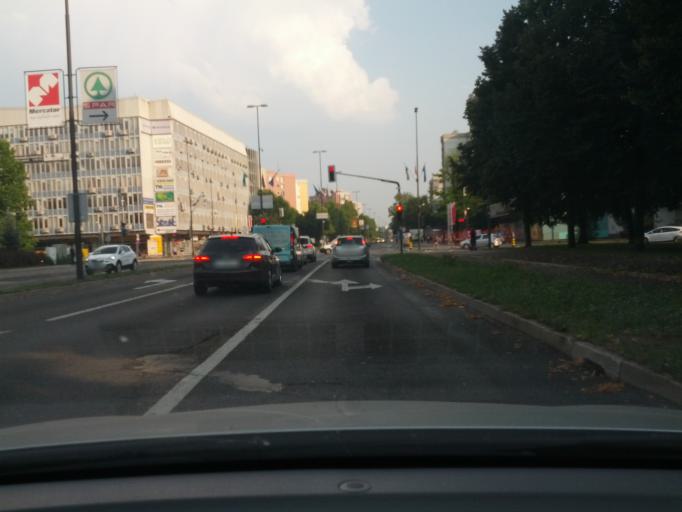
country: SI
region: Ljubljana
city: Ljubljana
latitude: 46.0743
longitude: 14.4851
